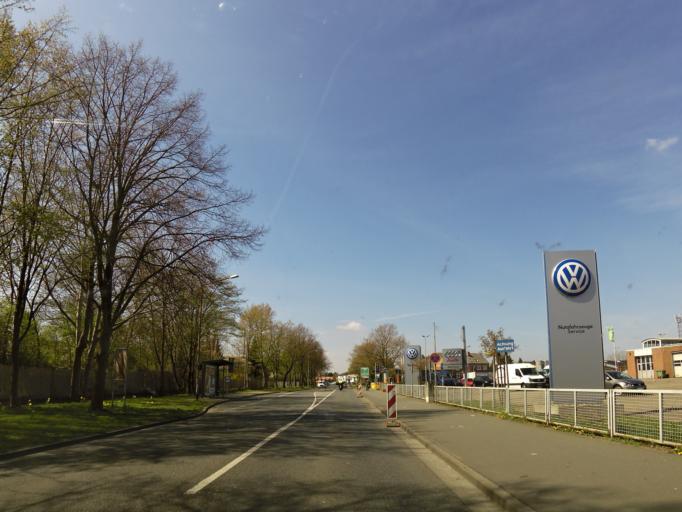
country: DE
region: Lower Saxony
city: Wunstorf
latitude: 52.4294
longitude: 9.4206
